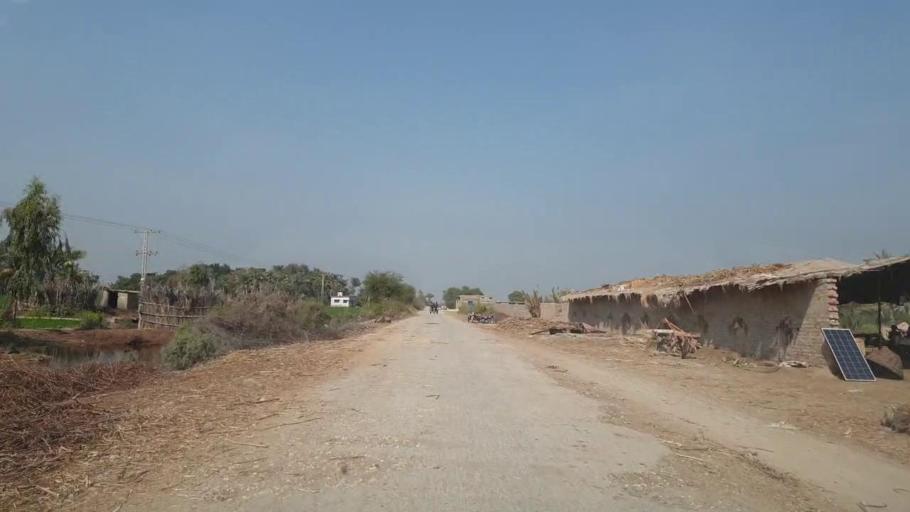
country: PK
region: Sindh
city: Mirpur Khas
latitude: 25.6845
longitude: 69.1552
